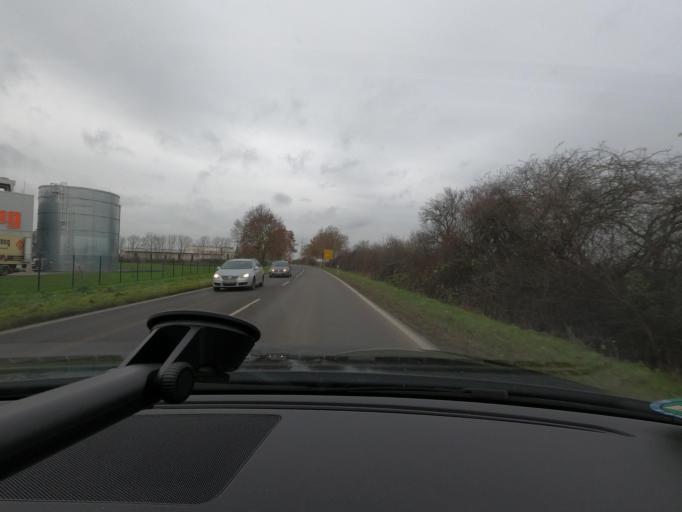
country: DE
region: North Rhine-Westphalia
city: Kempen
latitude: 51.3770
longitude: 6.4350
